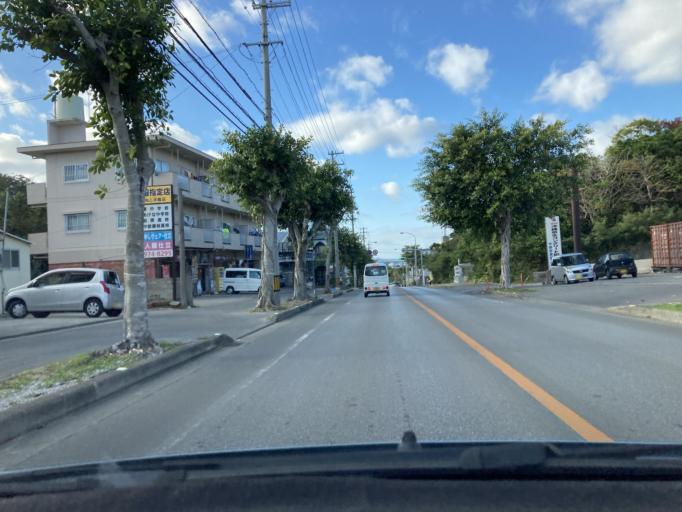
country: JP
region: Okinawa
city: Gushikawa
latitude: 26.3617
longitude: 127.8599
